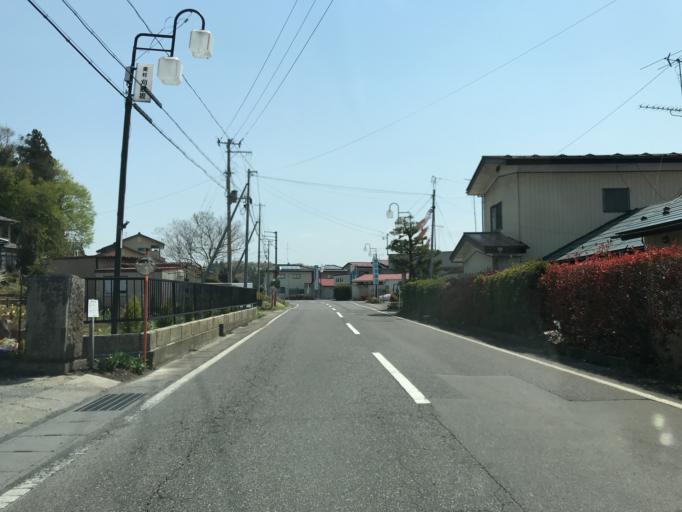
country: JP
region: Fukushima
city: Ishikawa
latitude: 37.1165
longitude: 140.3524
